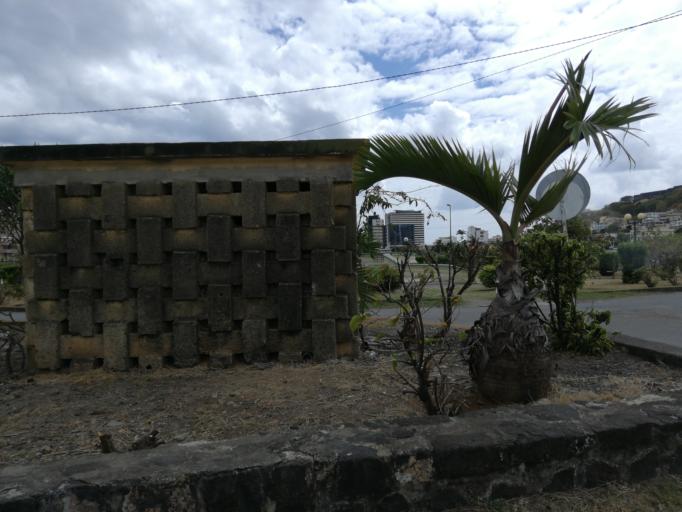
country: MU
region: Port Louis
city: Port Louis
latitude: -20.1696
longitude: 57.5103
